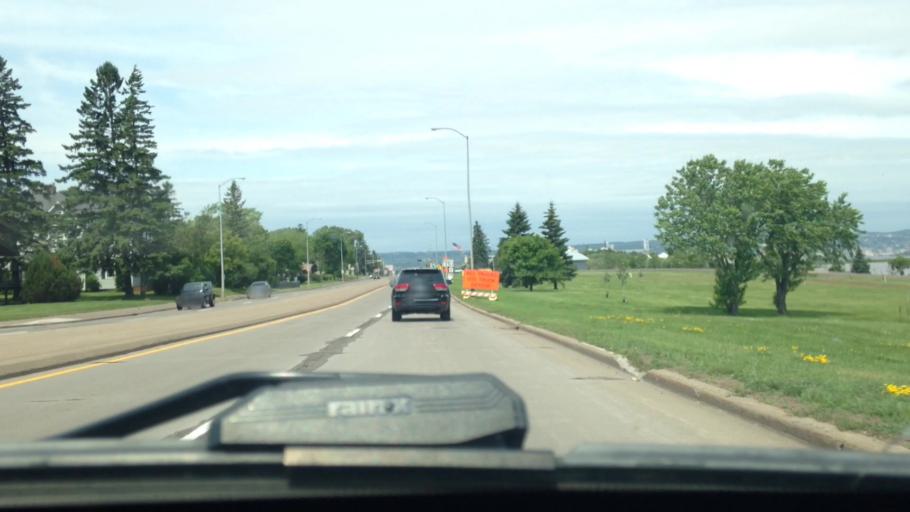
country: US
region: Wisconsin
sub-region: Douglas County
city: Superior
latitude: 46.7199
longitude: -92.0649
